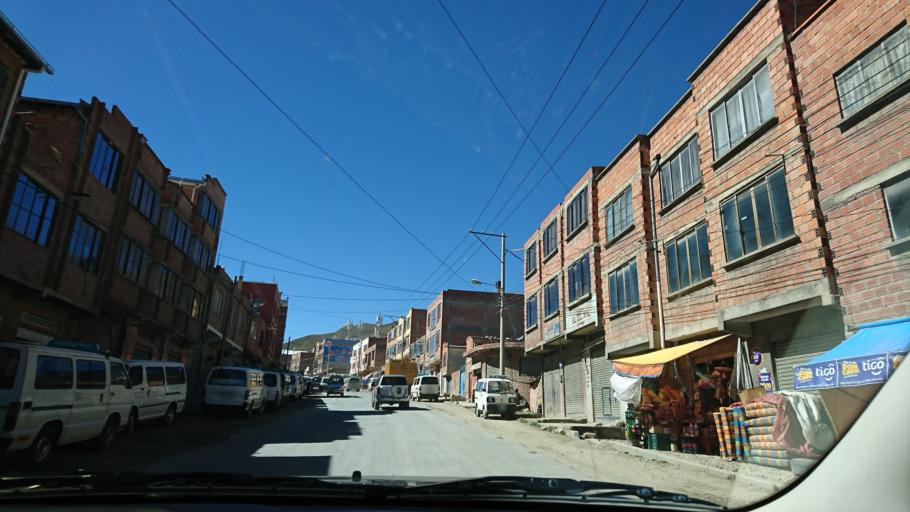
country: BO
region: La Paz
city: La Paz
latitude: -16.4521
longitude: -68.0928
